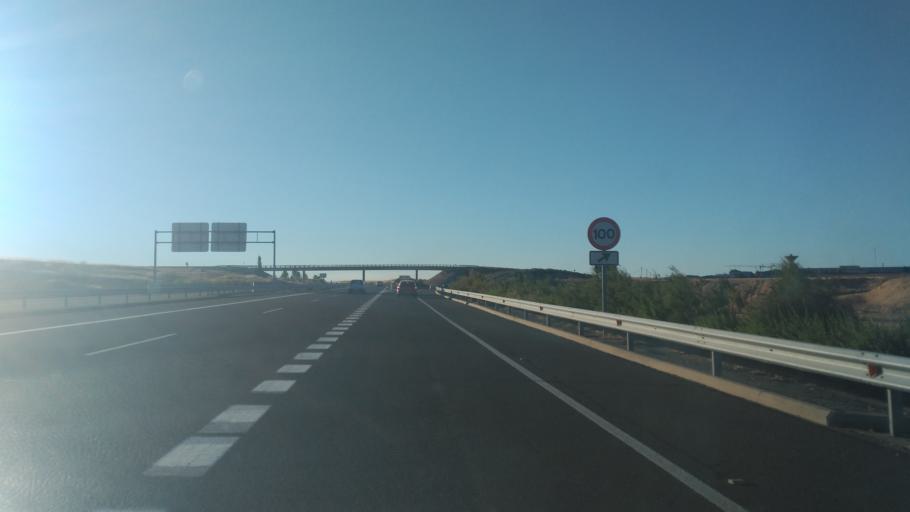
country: ES
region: Castille and Leon
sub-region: Provincia de Salamanca
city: Carbajosa de la Sagrada
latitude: 40.9199
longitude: -5.6654
